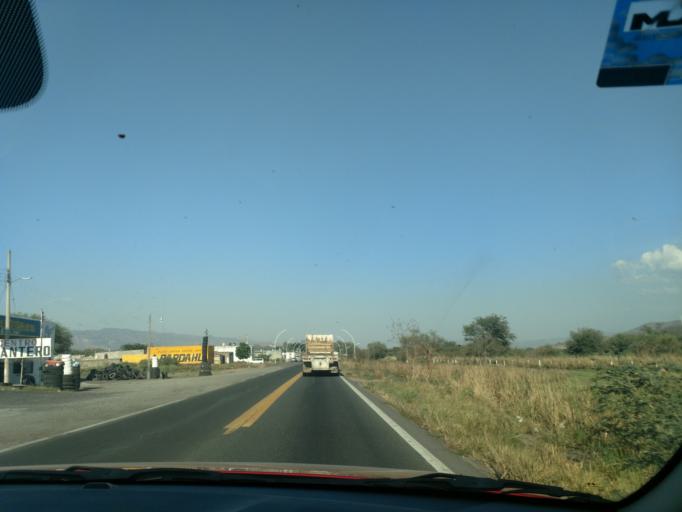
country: MX
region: Nayarit
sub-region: Ahuacatlan
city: Ahuacatlan
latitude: 21.0590
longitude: -104.4966
